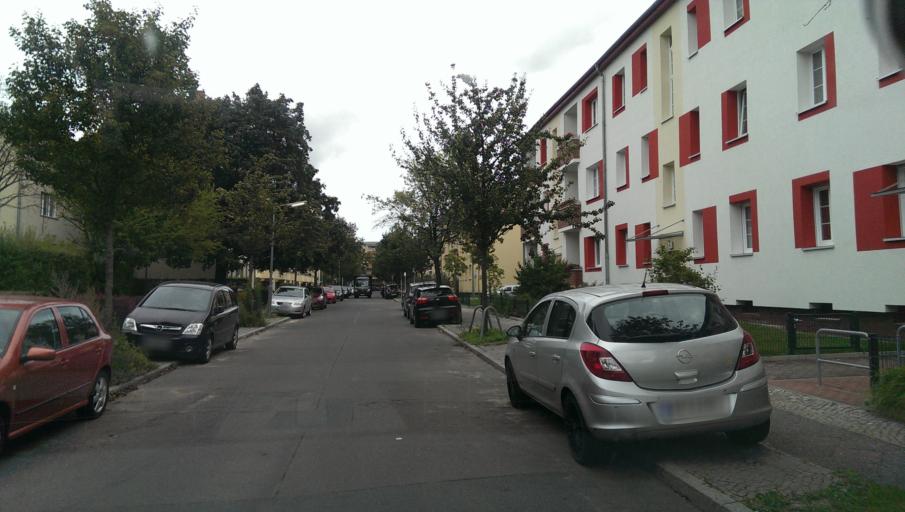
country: DE
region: Berlin
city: Mariendorf
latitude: 52.4454
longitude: 13.3984
